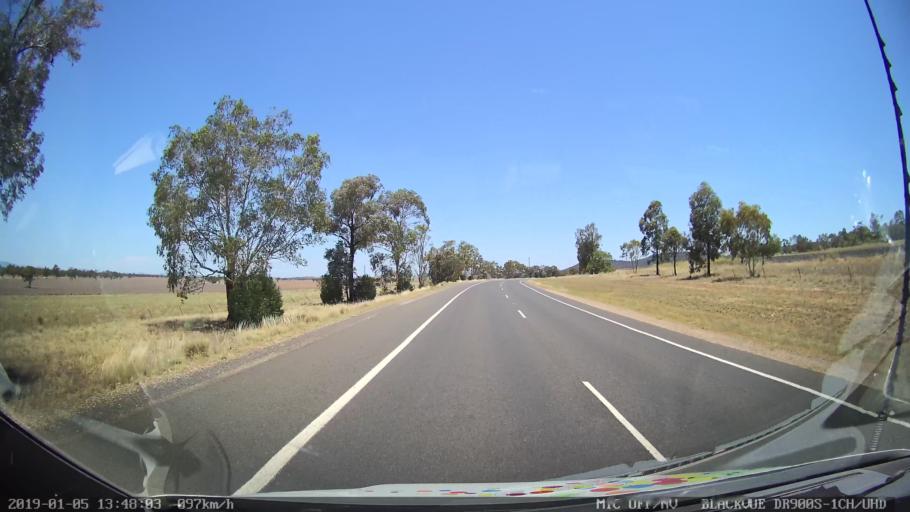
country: AU
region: New South Wales
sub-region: Gunnedah
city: Gunnedah
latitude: -30.9962
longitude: 150.2797
